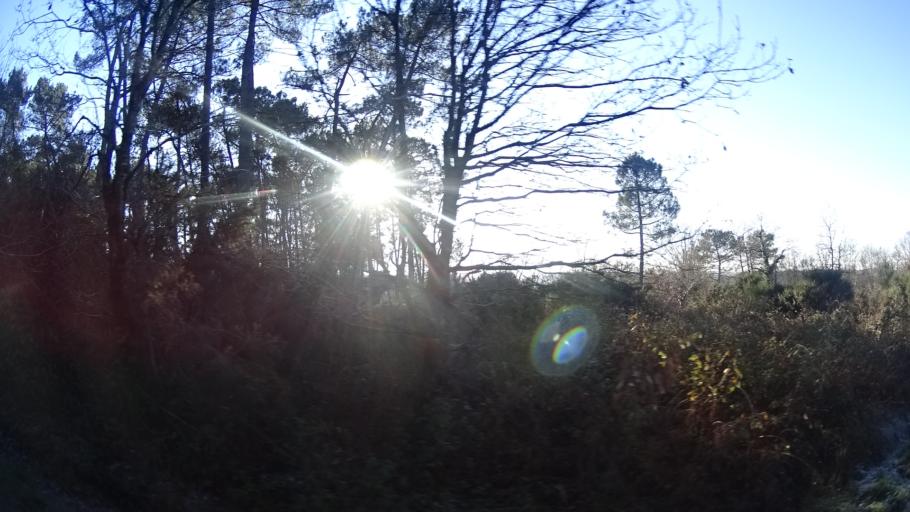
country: FR
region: Brittany
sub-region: Departement du Morbihan
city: Allaire
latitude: 47.6617
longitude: -2.1787
